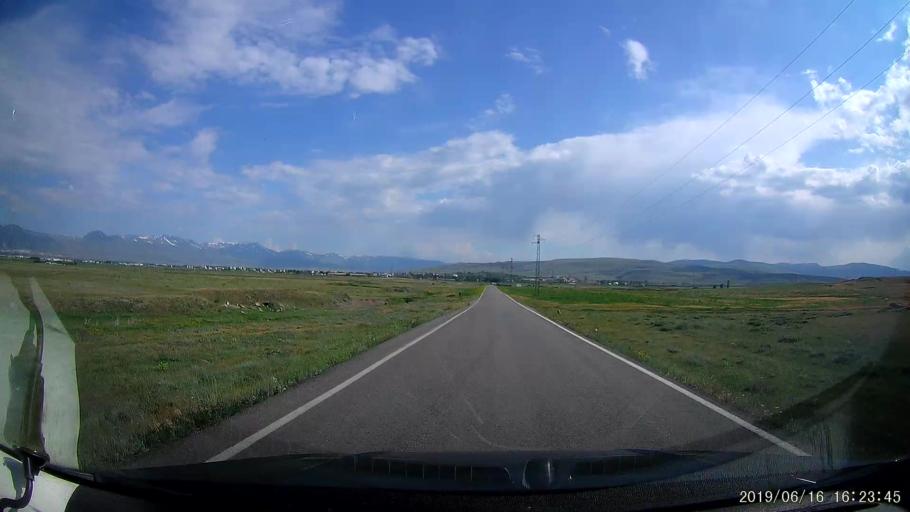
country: TR
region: Erzurum
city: Ilica
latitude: 39.9742
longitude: 41.1054
